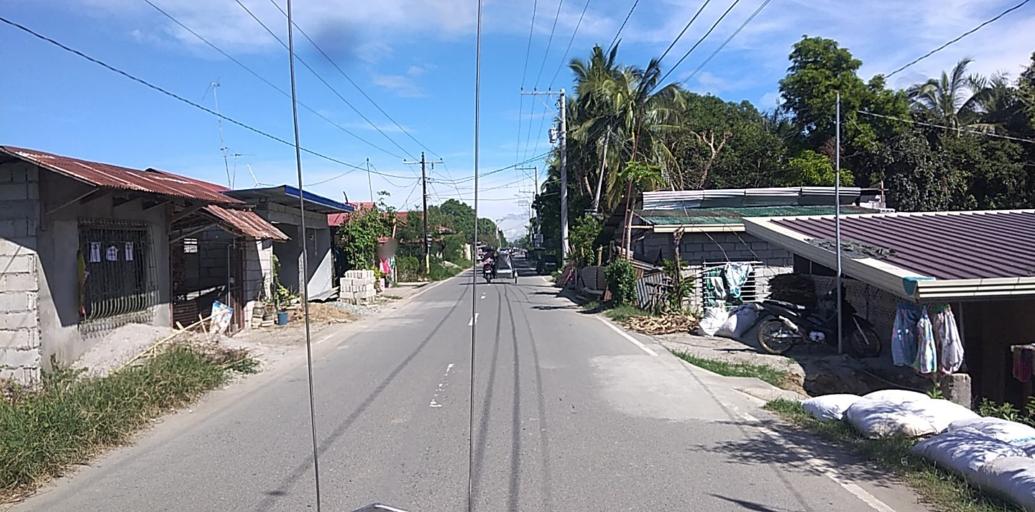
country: PH
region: Central Luzon
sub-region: Province of Pampanga
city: Candaba
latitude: 15.0902
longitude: 120.8115
